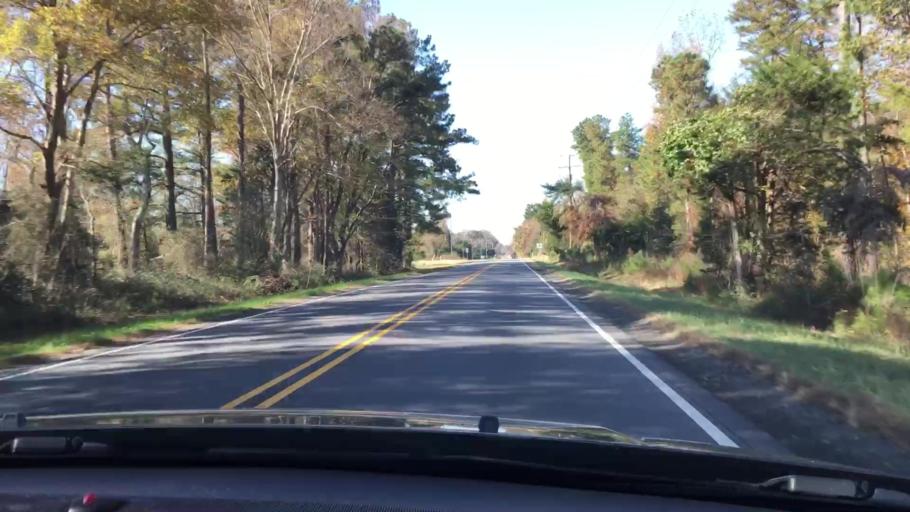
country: US
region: Virginia
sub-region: King William County
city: King William
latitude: 37.7019
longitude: -77.0444
